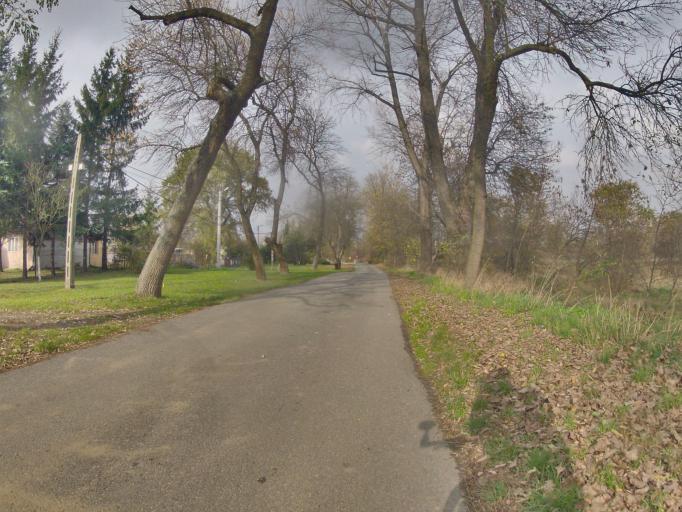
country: PL
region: Lesser Poland Voivodeship
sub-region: Powiat wielicki
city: Wegrzce Wielkie
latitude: 50.0570
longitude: 20.1119
